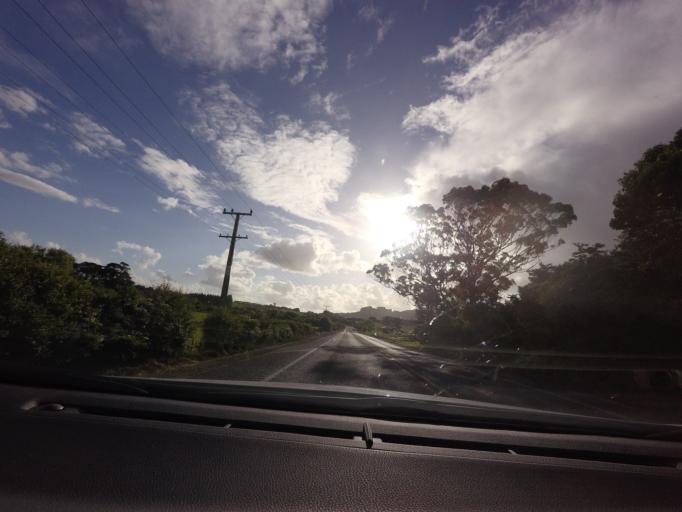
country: NZ
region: Auckland
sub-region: Auckland
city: Pukekohe East
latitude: -37.2172
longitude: 175.0526
